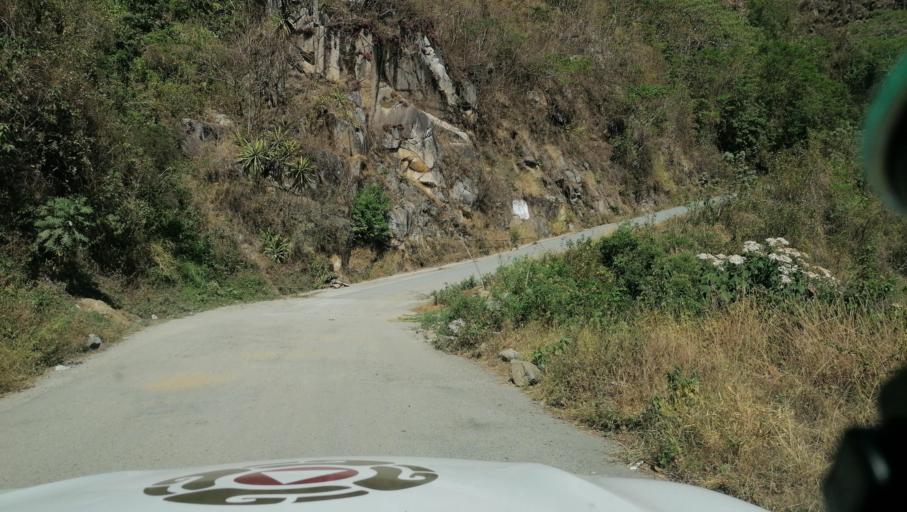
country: GT
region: San Marcos
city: Tacana
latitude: 15.1883
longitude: -92.1861
